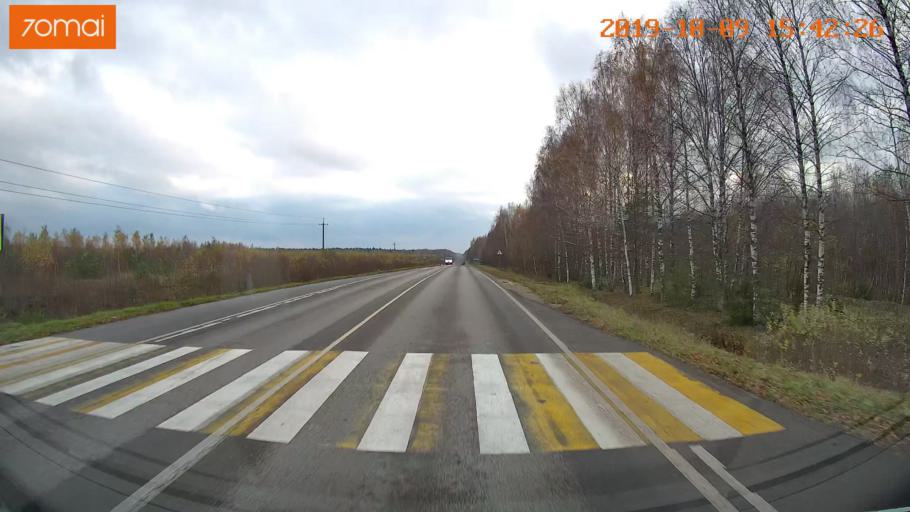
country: RU
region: Kostroma
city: Oktyabr'skiy
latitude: 57.8684
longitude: 41.1070
